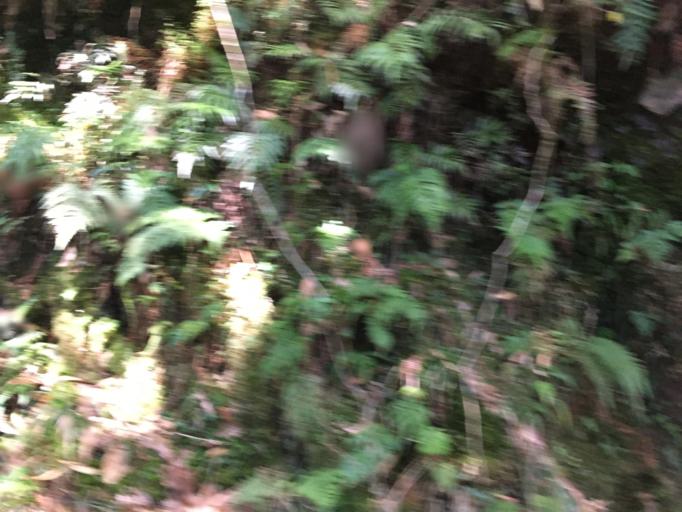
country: TW
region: Taiwan
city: Daxi
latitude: 24.5687
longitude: 121.4158
